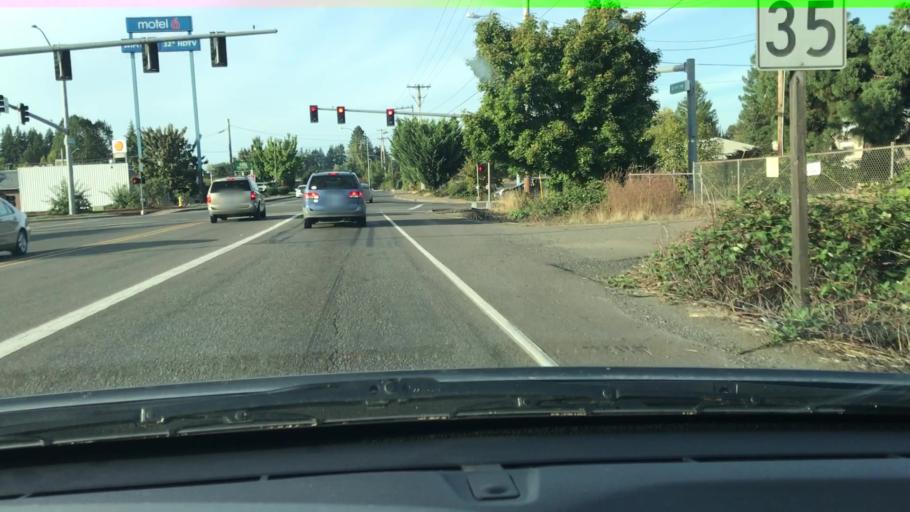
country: US
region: Oregon
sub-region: Yamhill County
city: McMinnville
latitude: 45.1924
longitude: -123.2100
